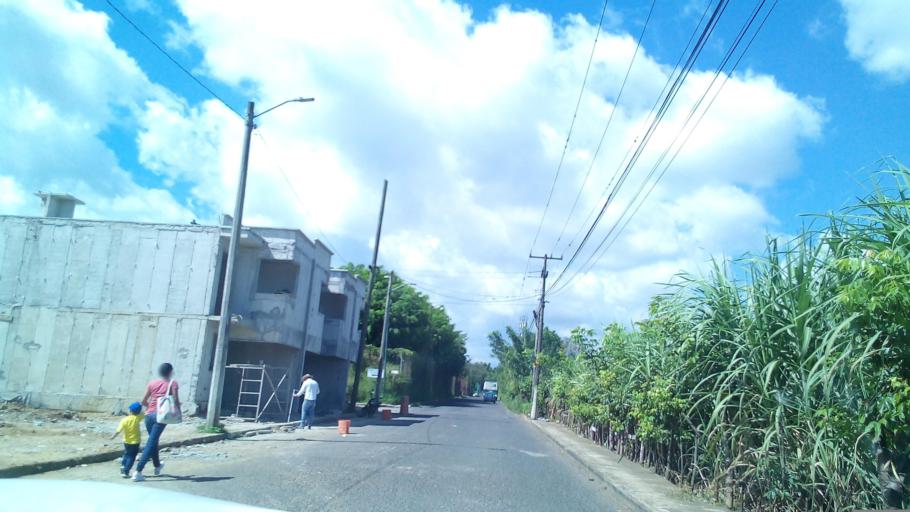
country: MX
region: Veracruz
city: Cordoba
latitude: 18.8677
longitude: -96.9242
